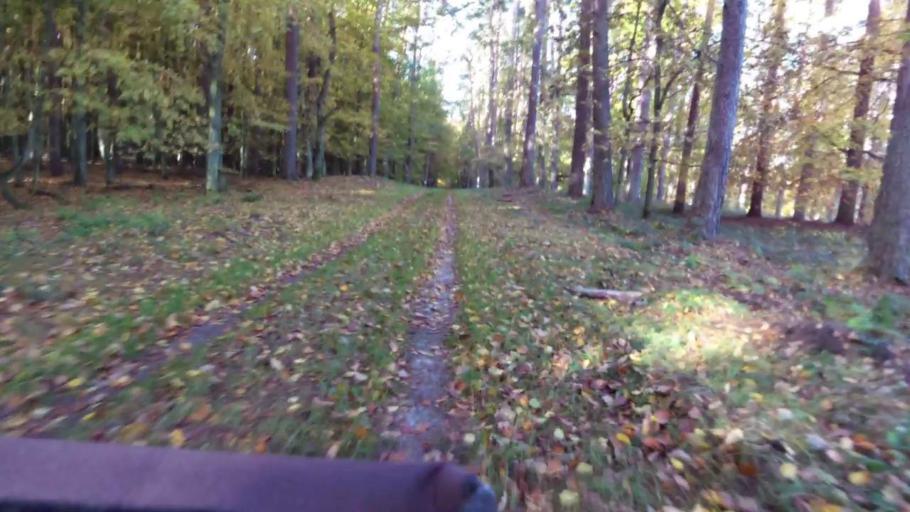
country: PL
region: West Pomeranian Voivodeship
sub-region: Powiat kamienski
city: Miedzyzdroje
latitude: 53.8644
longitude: 14.5158
